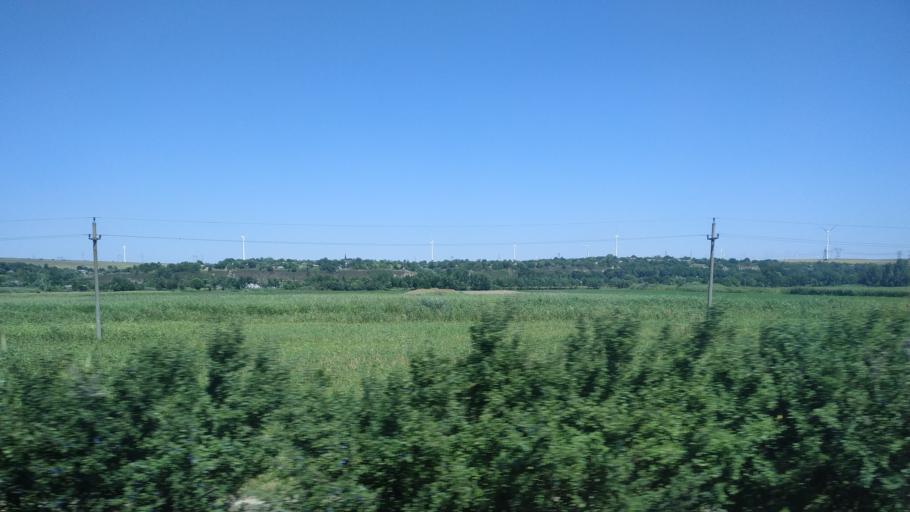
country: RO
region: Constanta
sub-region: Comuna Saligny
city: Faclia
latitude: 44.2724
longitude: 28.1050
